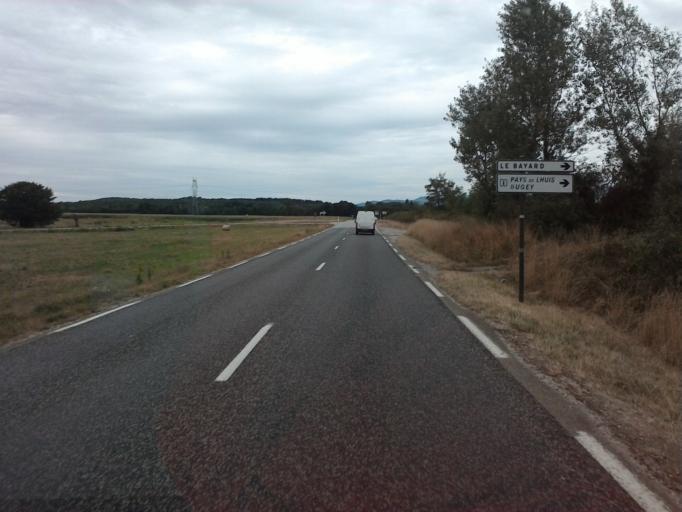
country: FR
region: Rhone-Alpes
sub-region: Departement de l'Isere
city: Bouvesse-Quirieu
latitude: 45.7483
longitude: 5.4042
